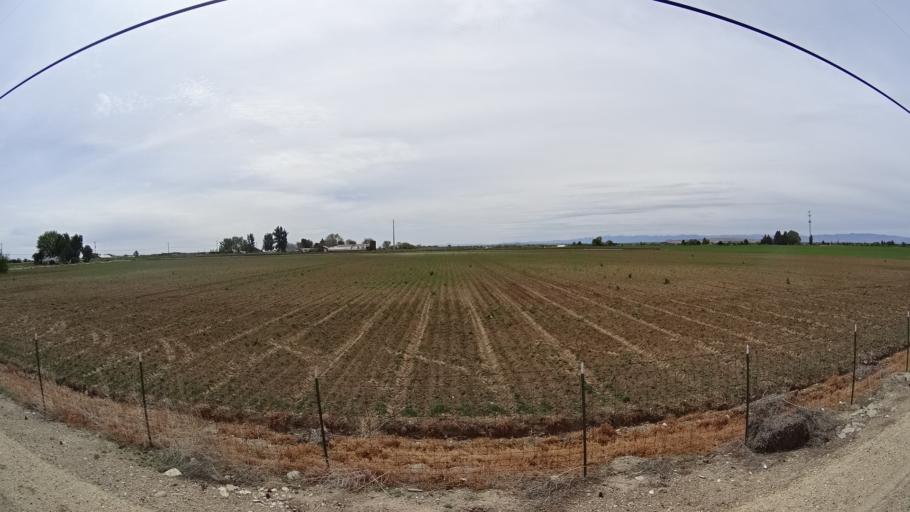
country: US
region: Idaho
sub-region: Ada County
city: Kuna
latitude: 43.5319
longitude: -116.3565
